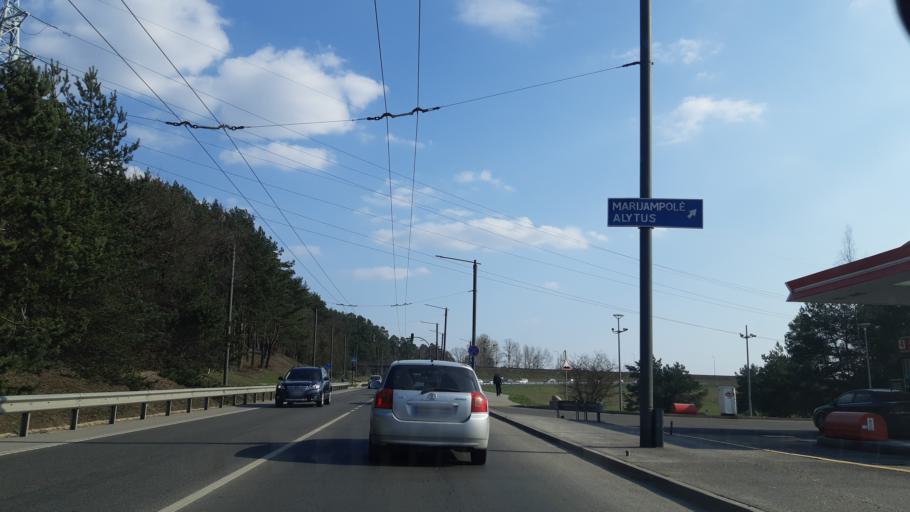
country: LT
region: Kauno apskritis
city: Dainava (Kaunas)
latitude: 54.8812
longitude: 24.0098
